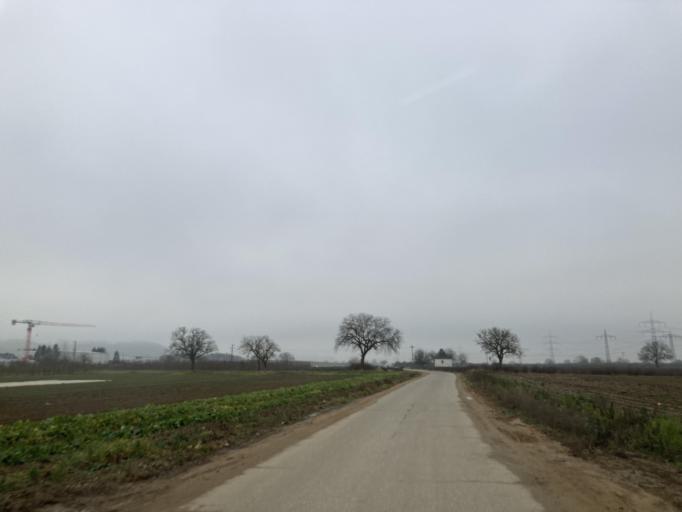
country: DE
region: Baden-Wuerttemberg
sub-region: Freiburg Region
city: Auggen
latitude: 47.7932
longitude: 7.5859
